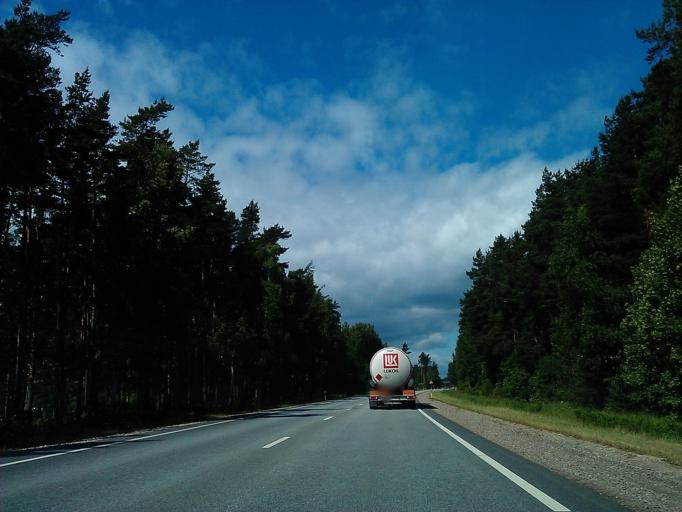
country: LV
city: Tireli
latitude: 56.9271
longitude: 23.6630
